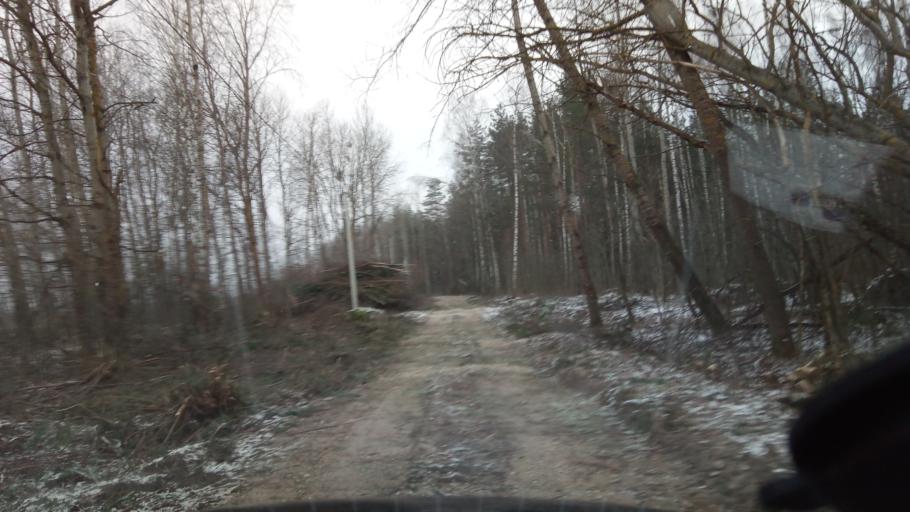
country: LT
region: Alytaus apskritis
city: Varena
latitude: 54.1311
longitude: 24.7033
